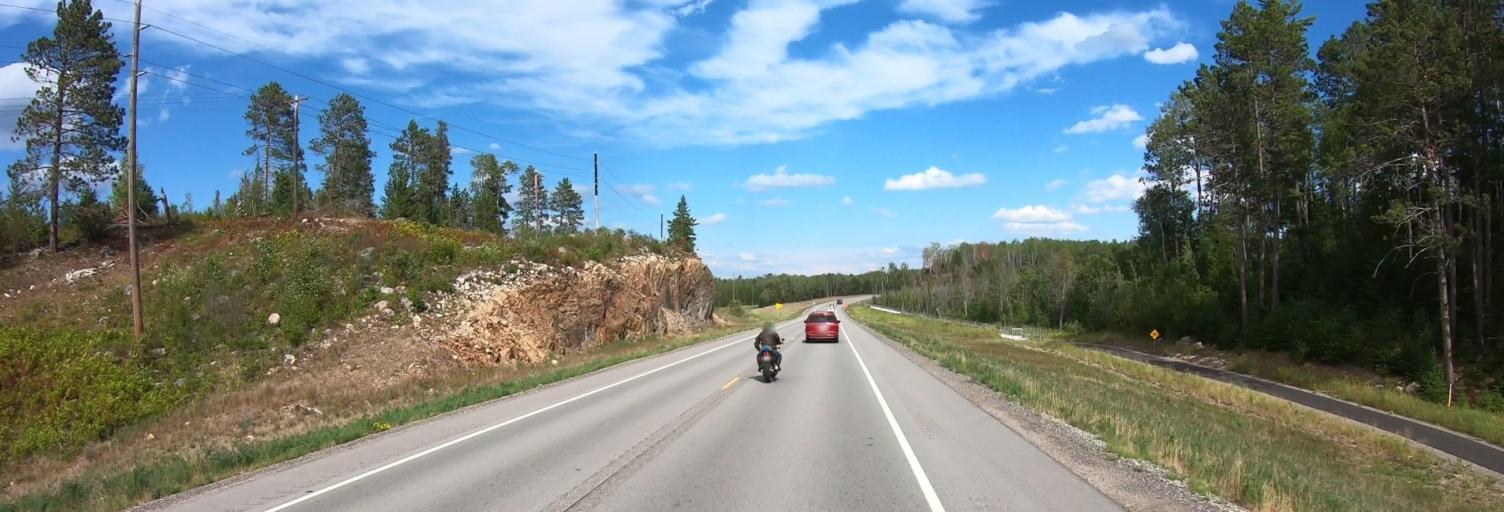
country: US
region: Minnesota
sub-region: Saint Louis County
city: Babbitt
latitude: 47.8475
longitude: -92.1180
